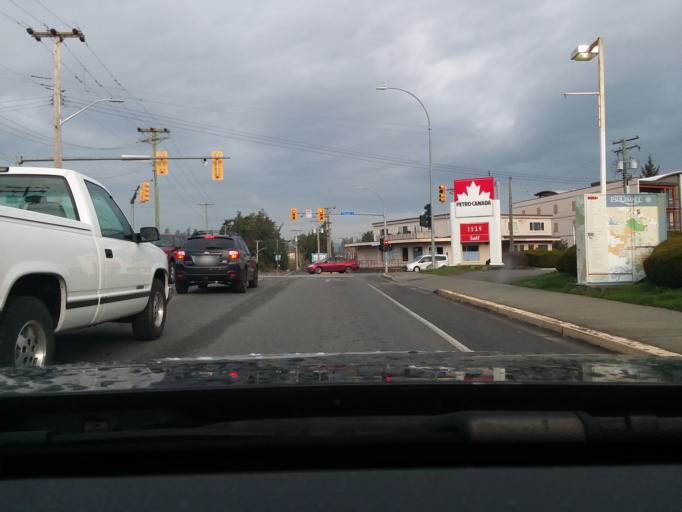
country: CA
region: British Columbia
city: Victoria
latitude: 48.4417
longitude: -123.4016
